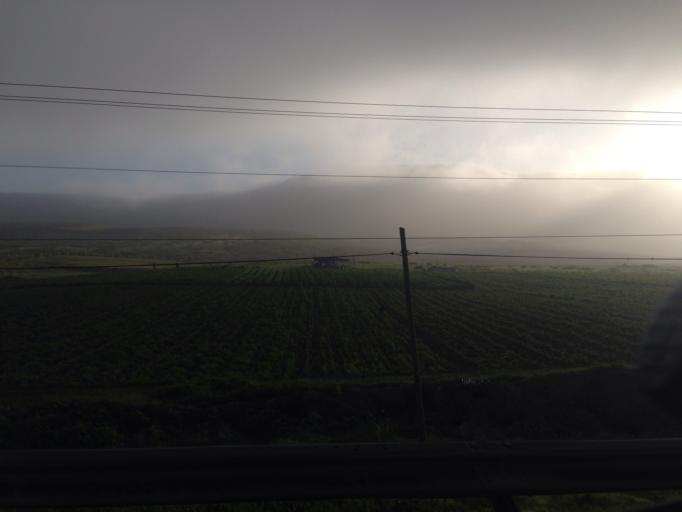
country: MX
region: Baja California
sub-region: Playas de Rosarito
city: Santa Anita
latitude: 32.0771
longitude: -116.8791
